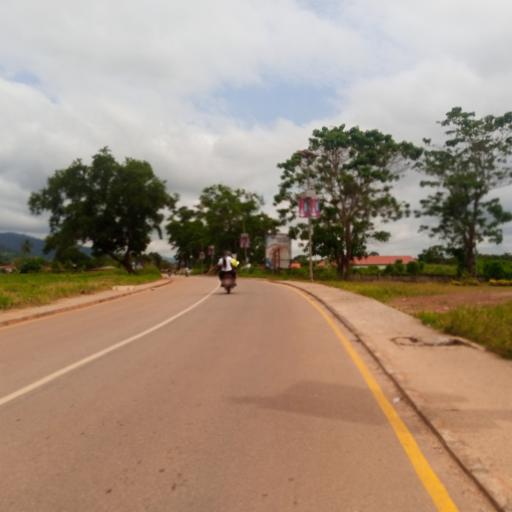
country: SL
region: Eastern Province
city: Kenema
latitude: 7.8556
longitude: -11.2047
